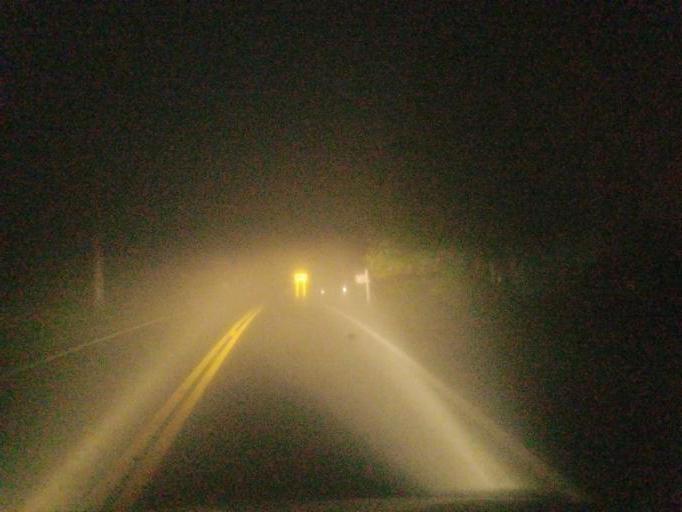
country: US
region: Ohio
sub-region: Knox County
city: Oak Hill
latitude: 40.2903
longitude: -82.1616
